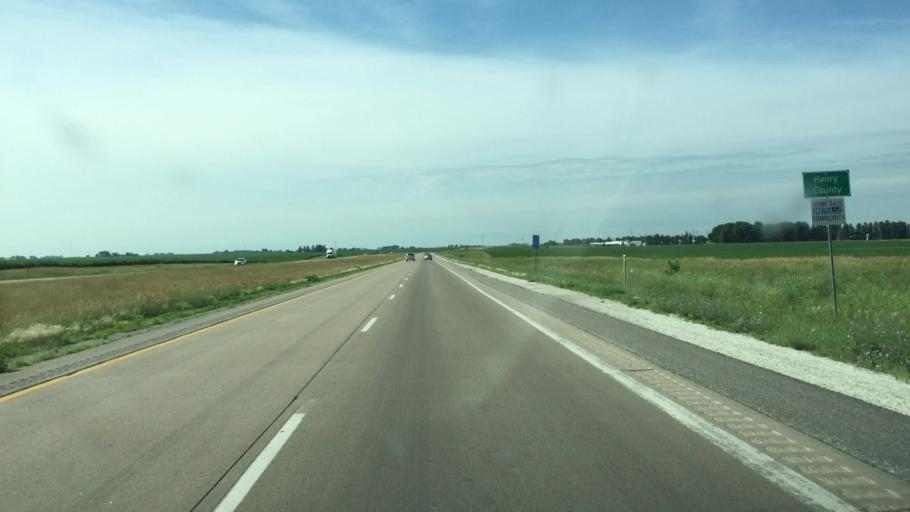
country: US
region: Iowa
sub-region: Henry County
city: Winfield
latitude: 41.1622
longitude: -91.5421
